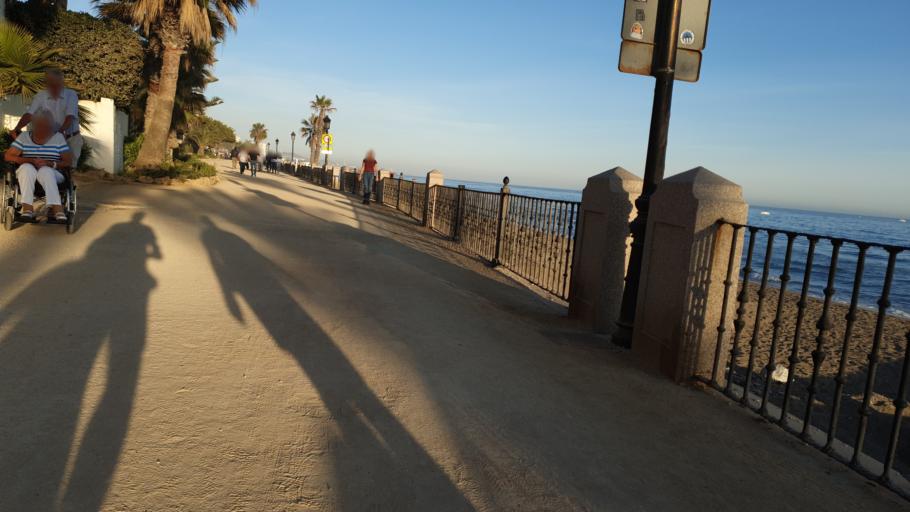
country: ES
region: Andalusia
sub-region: Provincia de Malaga
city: Marbella
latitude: 36.5061
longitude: -4.9094
